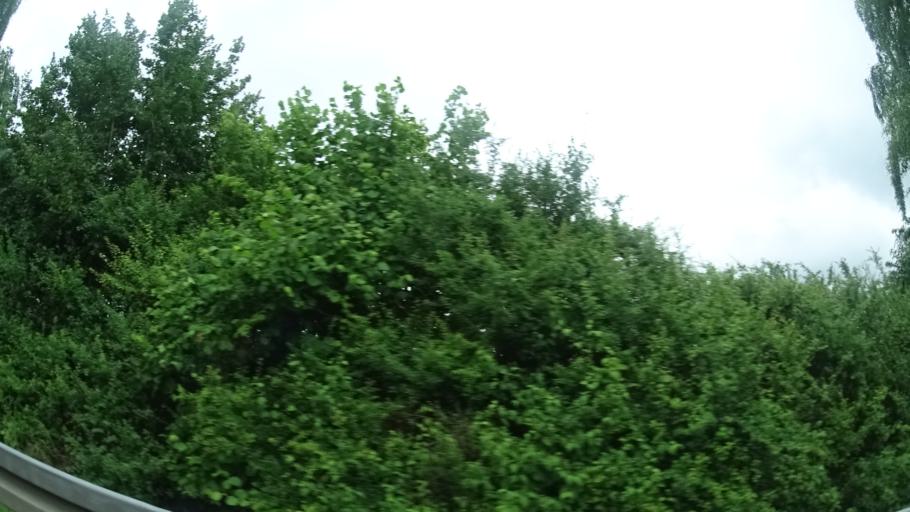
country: DE
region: Saarland
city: Orscholz
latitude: 49.4558
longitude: 6.5072
